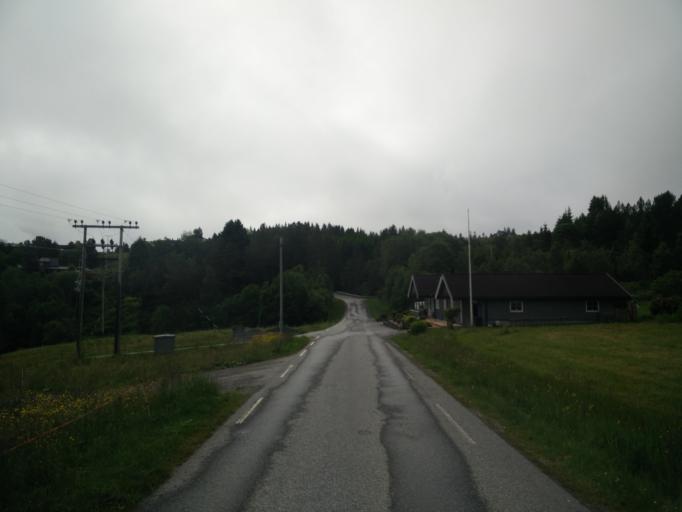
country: NO
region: More og Romsdal
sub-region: Kristiansund
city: Rensvik
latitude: 63.0171
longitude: 7.9632
